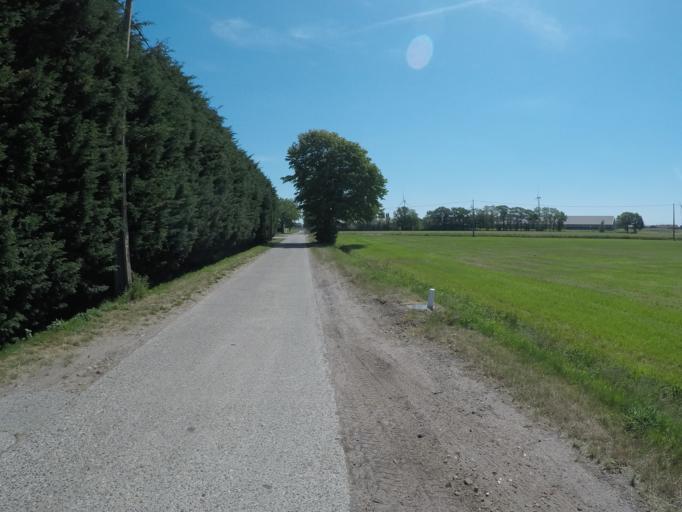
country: NL
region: North Brabant
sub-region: Gemeente Zundert
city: Zundert
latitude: 51.4094
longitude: 4.6681
